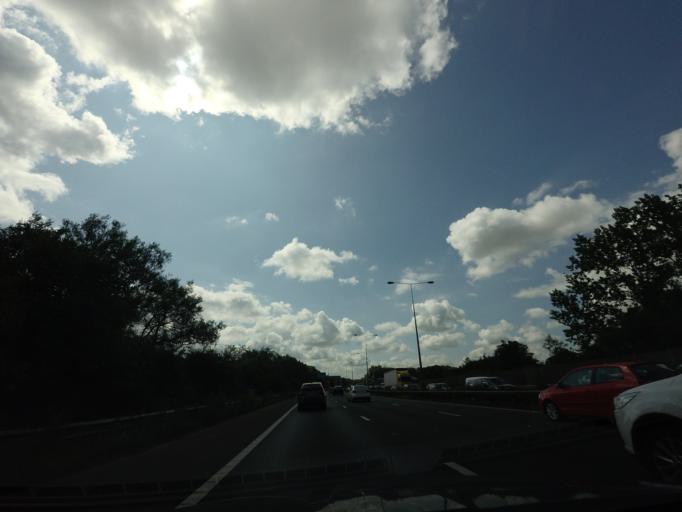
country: GB
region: England
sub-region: Lancashire
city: Clayton-le-Woods
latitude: 53.7253
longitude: -2.6519
